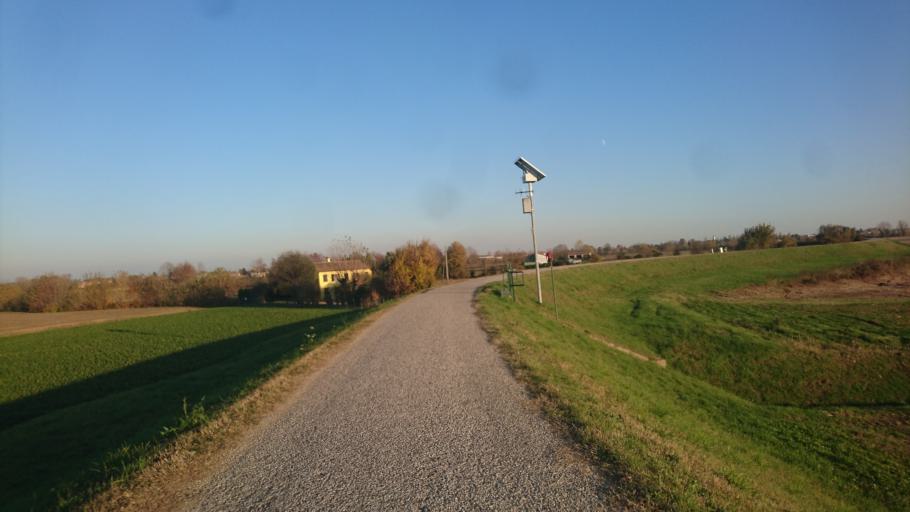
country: IT
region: Veneto
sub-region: Provincia di Padova
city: Saccolongo
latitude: 45.4042
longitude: 11.7625
